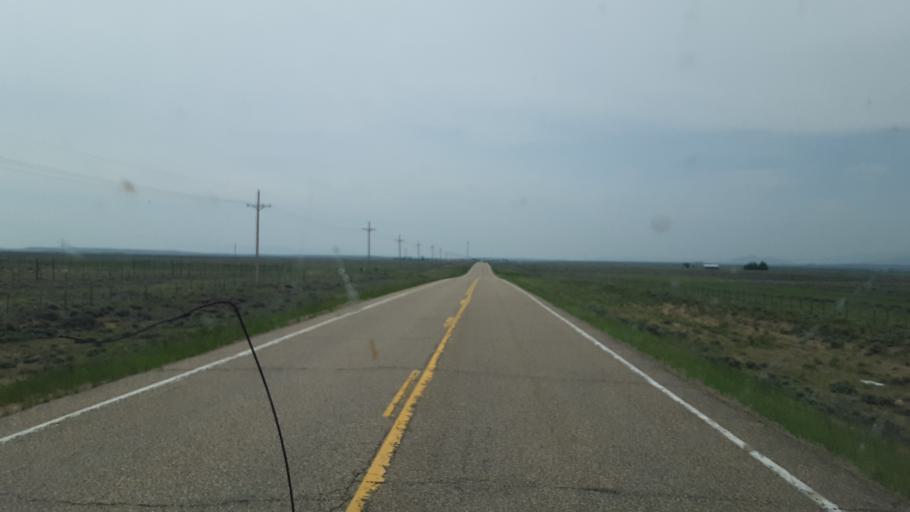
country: US
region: Colorado
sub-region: Jackson County
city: Walden
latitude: 40.8879
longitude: -106.3015
